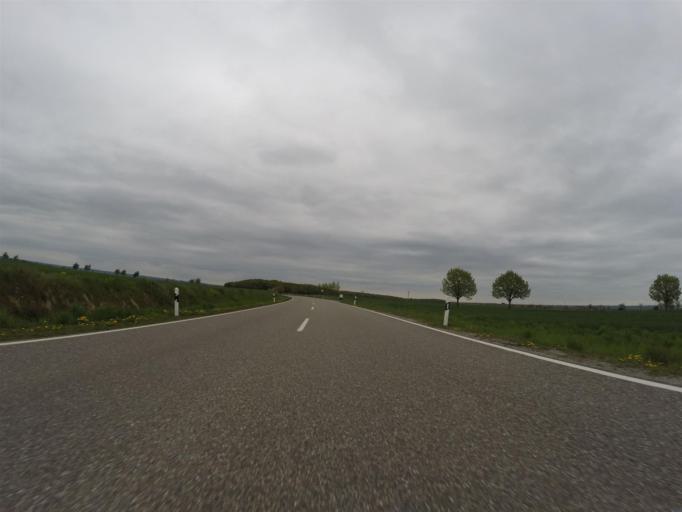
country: DE
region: Saxony-Anhalt
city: Naumburg
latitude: 51.1207
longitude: 11.7823
